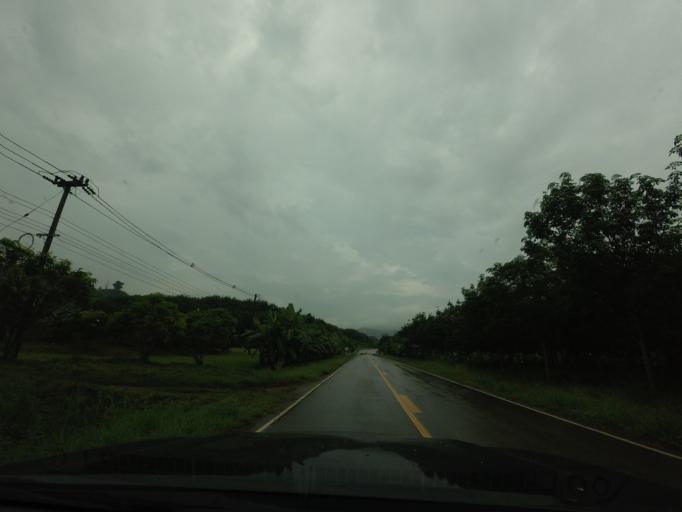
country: TH
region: Nong Khai
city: Sangkhom
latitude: 18.2119
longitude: 102.0870
